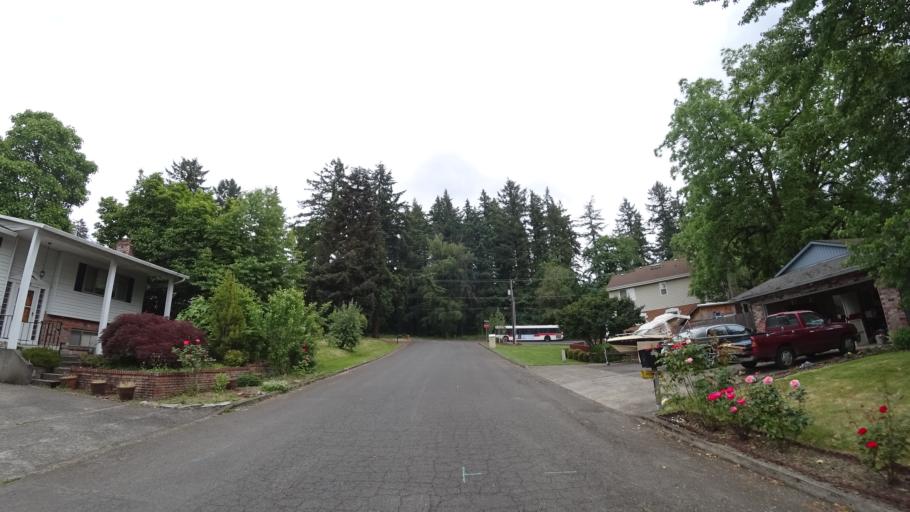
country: US
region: Oregon
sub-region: Multnomah County
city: Lents
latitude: 45.4653
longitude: -122.5568
